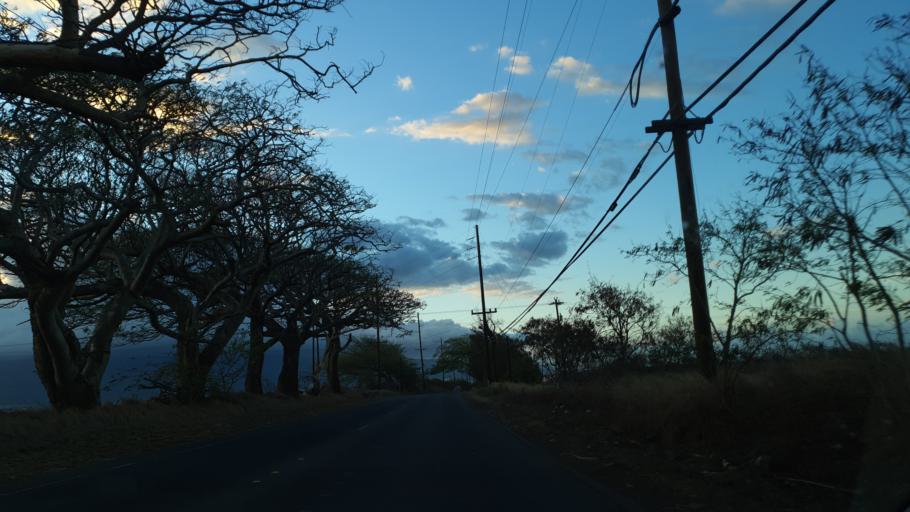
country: US
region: Hawaii
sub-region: Maui County
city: Kahului
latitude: 20.8672
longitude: -156.4339
